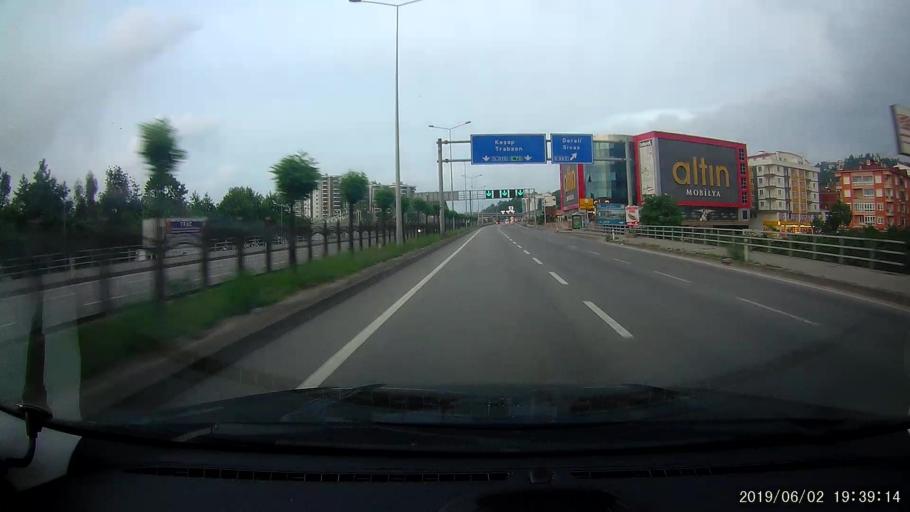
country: TR
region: Giresun
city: Giresun
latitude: 40.9123
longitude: 38.4371
